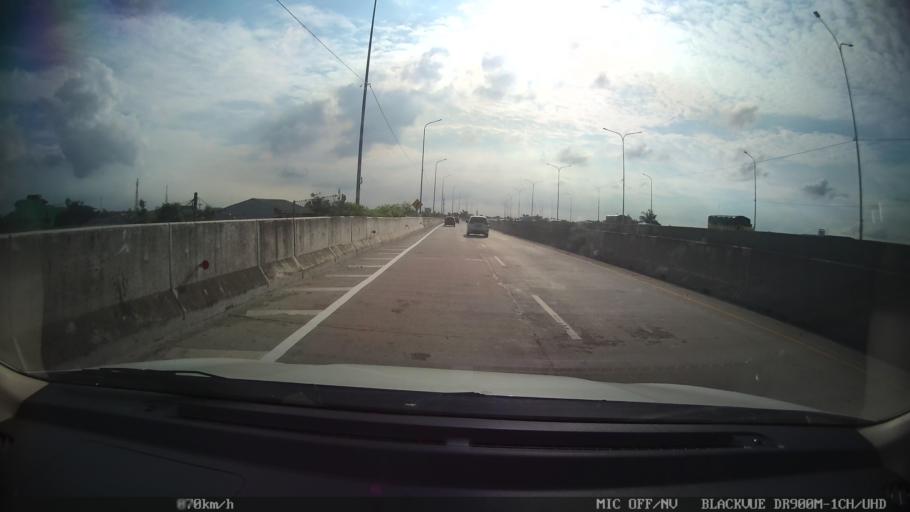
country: ID
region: North Sumatra
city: Medan
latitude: 3.6480
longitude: 98.6765
